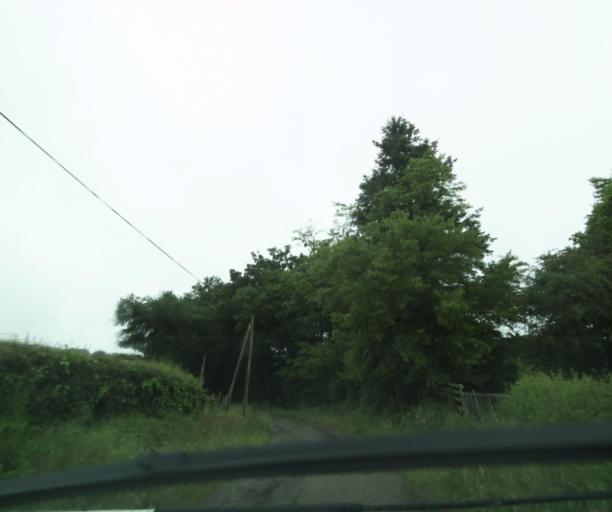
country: FR
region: Bourgogne
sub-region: Departement de Saone-et-Loire
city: Charolles
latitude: 46.3841
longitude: 4.3240
